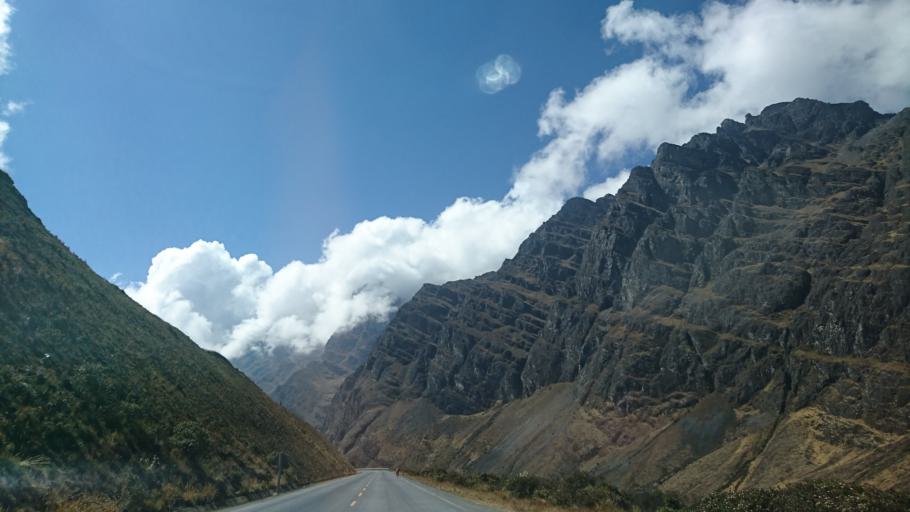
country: BO
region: La Paz
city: La Paz
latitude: -16.3310
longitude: -67.9829
